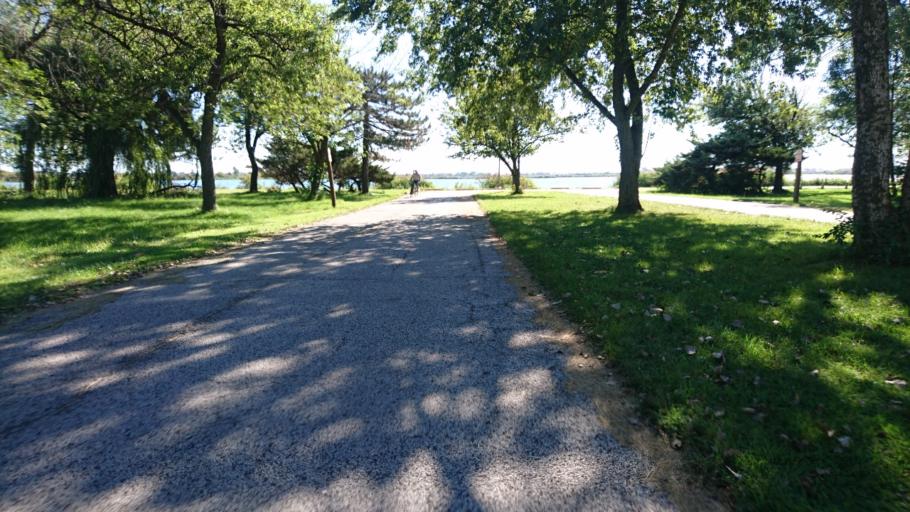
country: US
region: Illinois
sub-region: Cook County
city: Burnham
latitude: 41.6682
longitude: -87.5373
